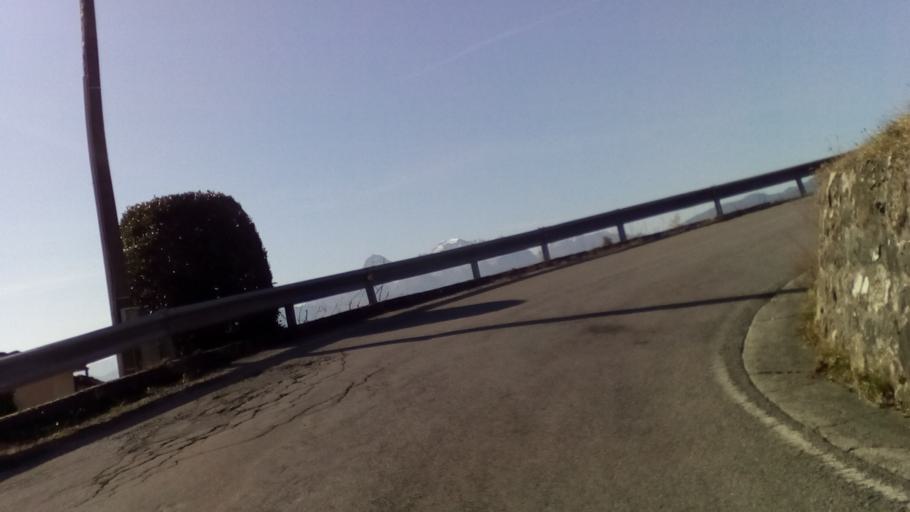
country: IT
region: Tuscany
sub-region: Provincia di Lucca
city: Castiglione di Garfagnana
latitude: 44.1415
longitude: 10.4259
